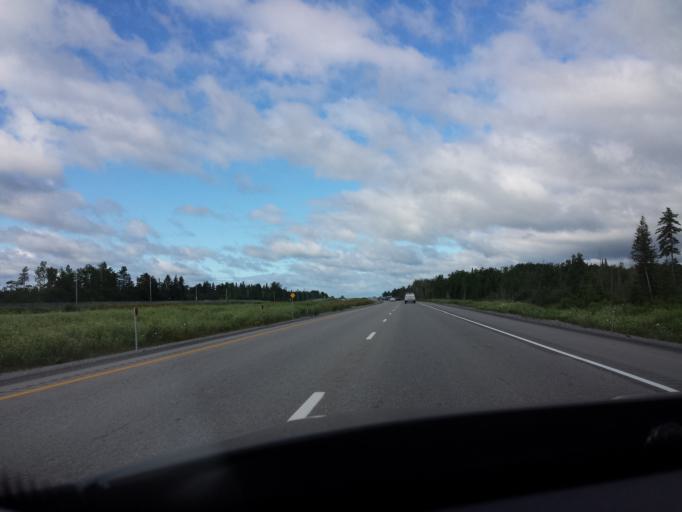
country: CA
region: Ontario
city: Carleton Place
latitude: 45.2215
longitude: -76.0109
